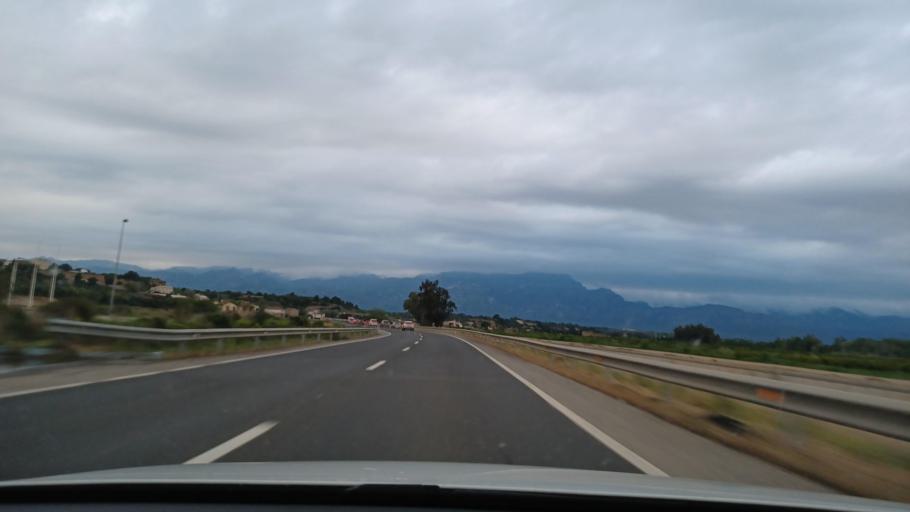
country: ES
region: Catalonia
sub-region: Provincia de Tarragona
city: Tortosa
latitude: 40.7756
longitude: 0.5216
